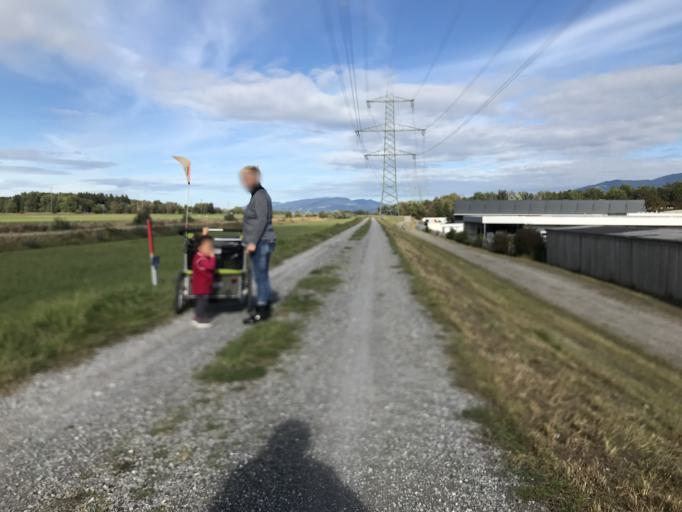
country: AT
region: Vorarlberg
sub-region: Politischer Bezirk Feldkirch
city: Mader
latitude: 47.3586
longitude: 9.6162
